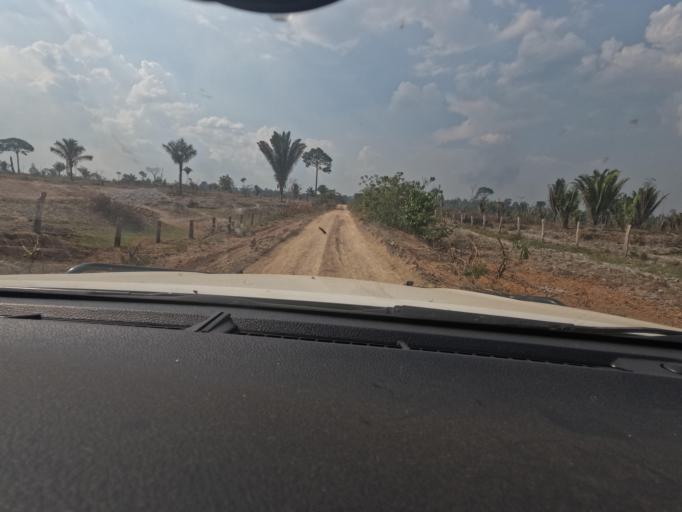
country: BR
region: Rondonia
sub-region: Porto Velho
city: Porto Velho
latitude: -8.6823
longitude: -63.1556
